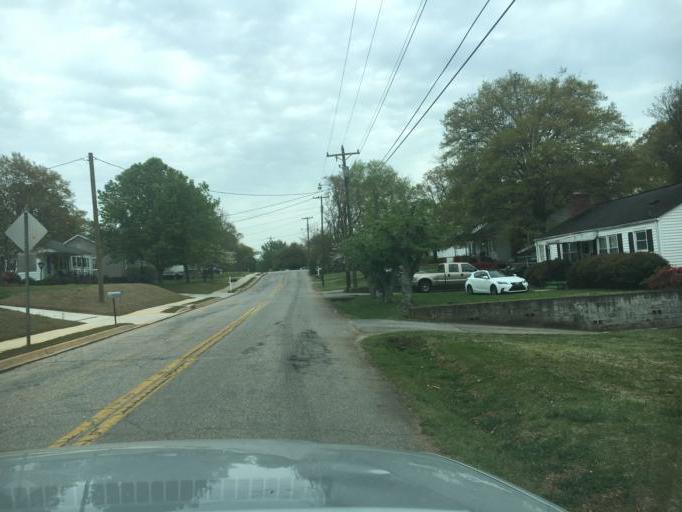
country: US
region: South Carolina
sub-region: Greenville County
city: Greenville
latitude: 34.8630
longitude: -82.3770
